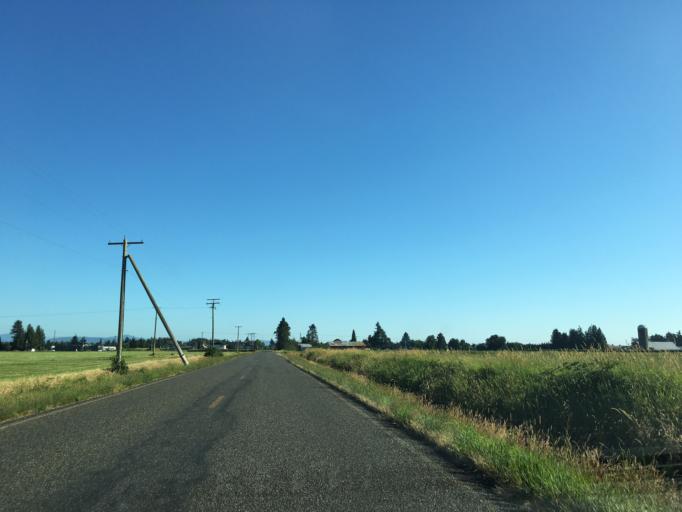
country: US
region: Washington
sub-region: Whatcom County
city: Lynden
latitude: 48.9695
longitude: -122.4521
